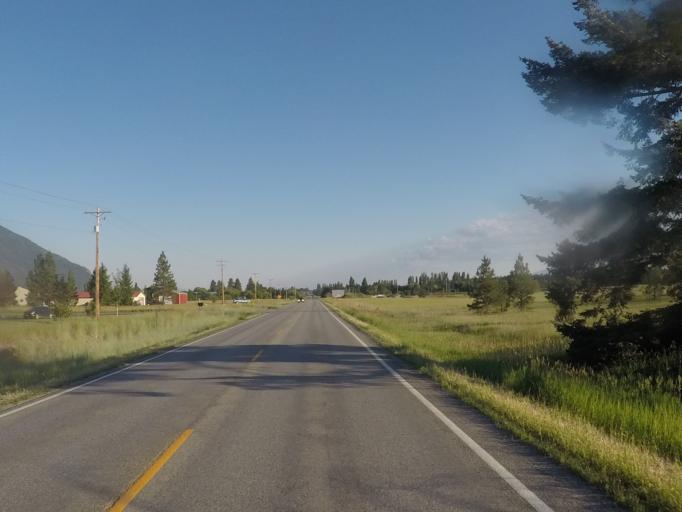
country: US
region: Montana
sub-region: Flathead County
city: Columbia Falls
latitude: 48.3499
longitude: -114.1593
